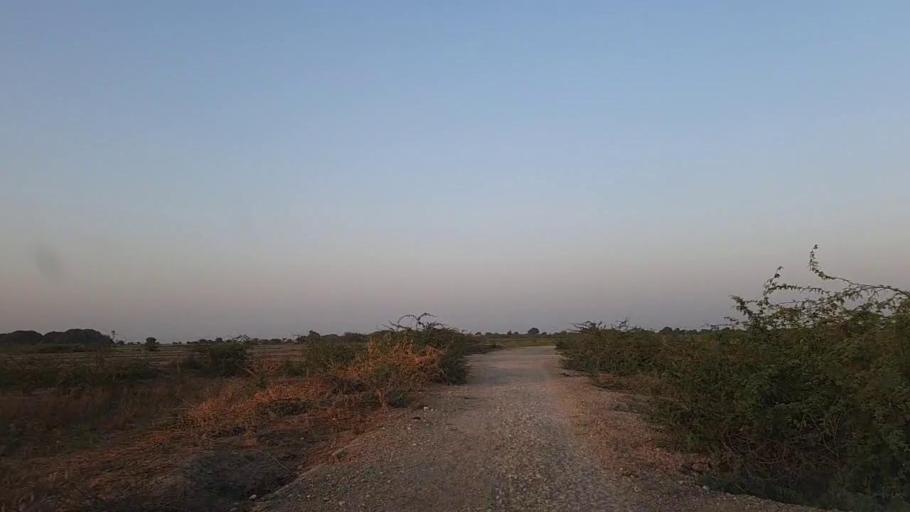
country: PK
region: Sindh
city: Naukot
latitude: 24.8787
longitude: 69.3518
